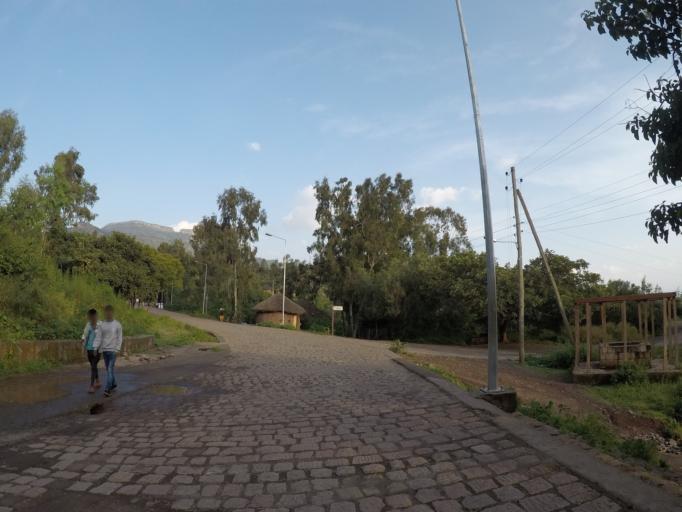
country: ET
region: Amhara
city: Lalibela
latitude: 12.0330
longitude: 39.0418
